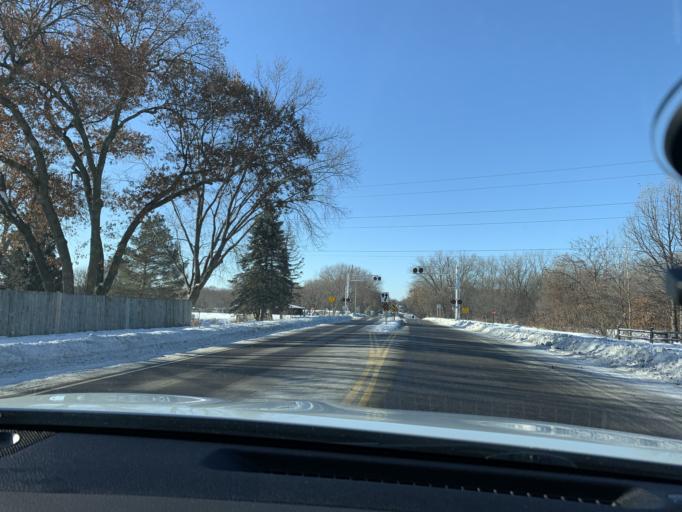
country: US
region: Minnesota
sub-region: Anoka County
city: Coon Rapids
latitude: 45.1625
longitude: -93.2930
